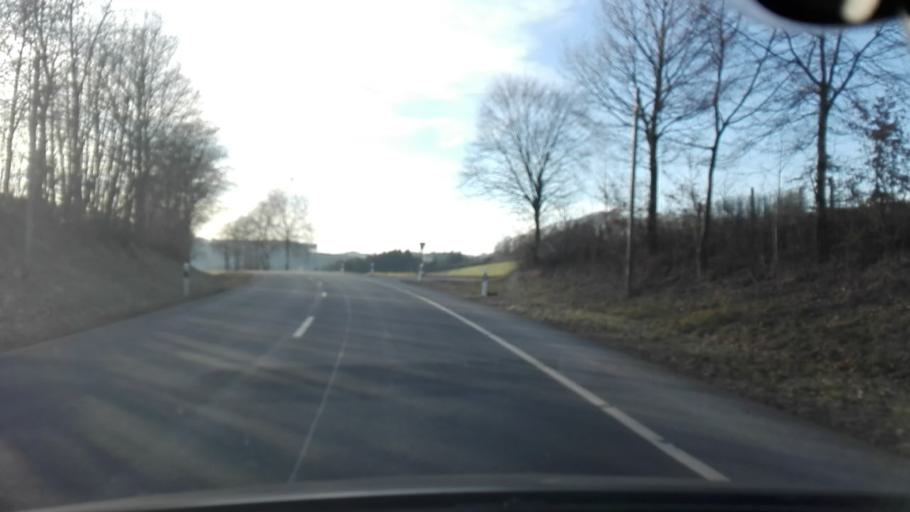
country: DE
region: North Rhine-Westphalia
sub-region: Regierungsbezirk Arnsberg
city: Schmallenberg
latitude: 51.1655
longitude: 8.2056
